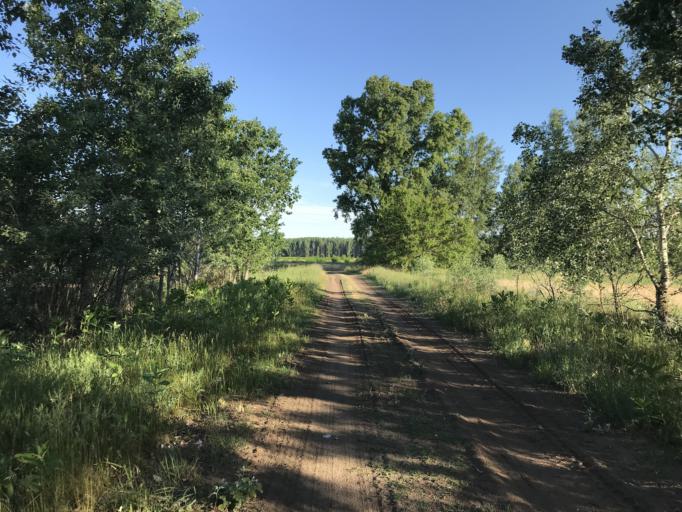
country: HU
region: Bacs-Kiskun
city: Tiszakecske
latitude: 46.9743
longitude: 20.0598
